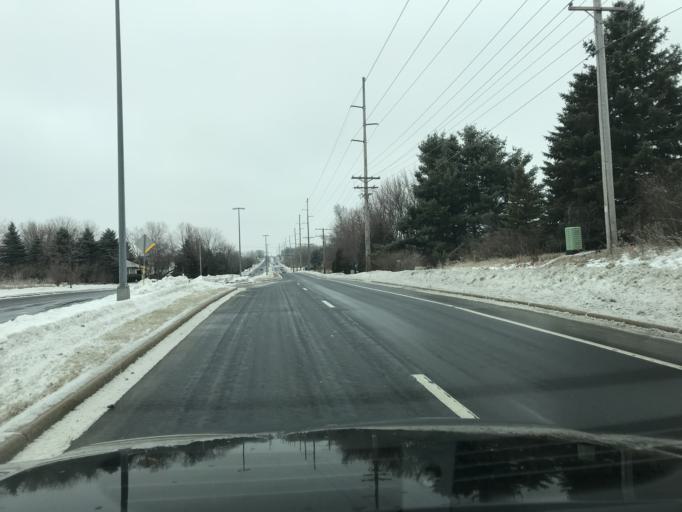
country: US
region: Wisconsin
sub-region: Dane County
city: Cottage Grove
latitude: 43.0989
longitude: -89.2667
